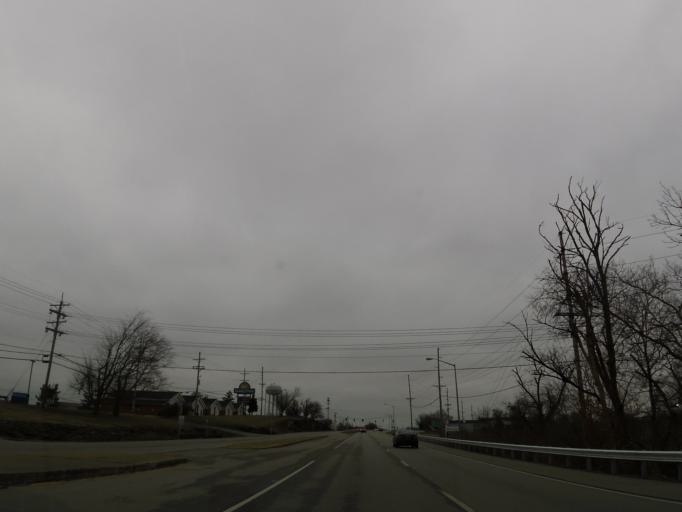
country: US
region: Kentucky
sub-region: Franklin County
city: Frankfort
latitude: 38.1784
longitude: -84.8951
